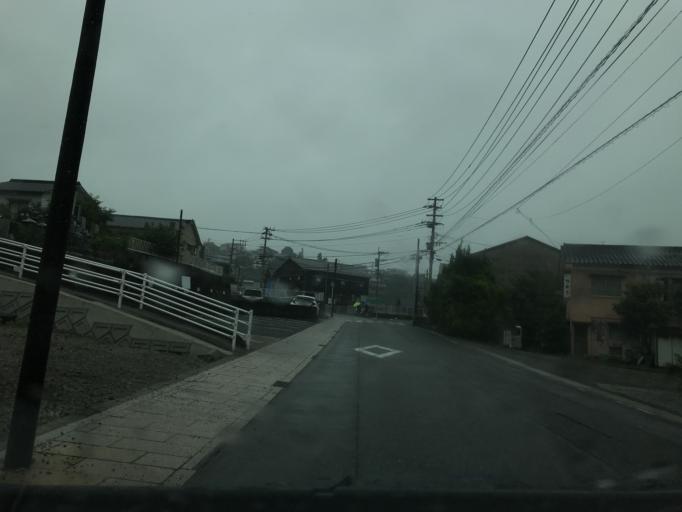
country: JP
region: Oita
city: Beppu
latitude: 33.3147
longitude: 131.4795
